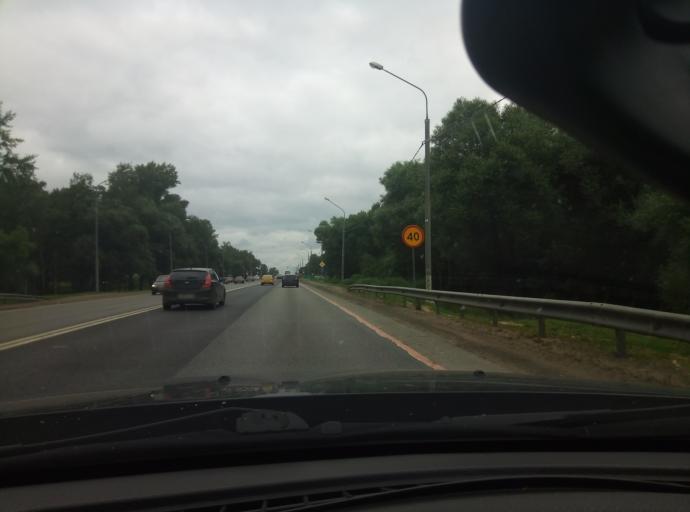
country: RU
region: Kaluga
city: Obninsk
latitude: 55.0979
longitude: 36.6381
